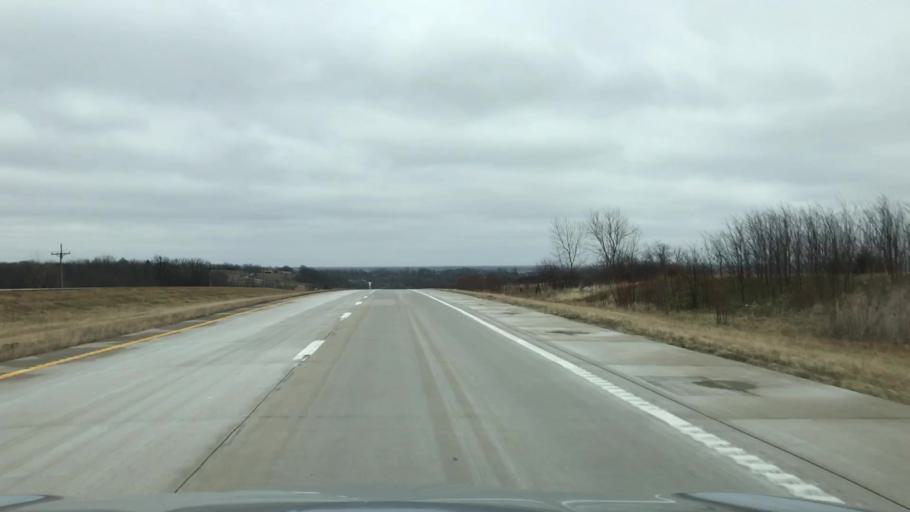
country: US
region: Missouri
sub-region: Livingston County
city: Chillicothe
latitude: 39.7395
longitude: -93.6576
